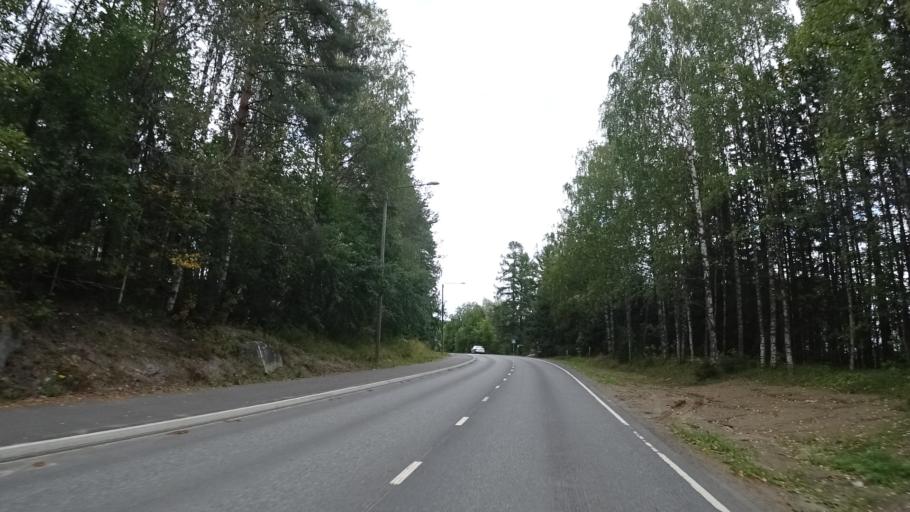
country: FI
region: North Karelia
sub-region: Joensuu
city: Ilomantsi
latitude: 62.6544
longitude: 30.9377
